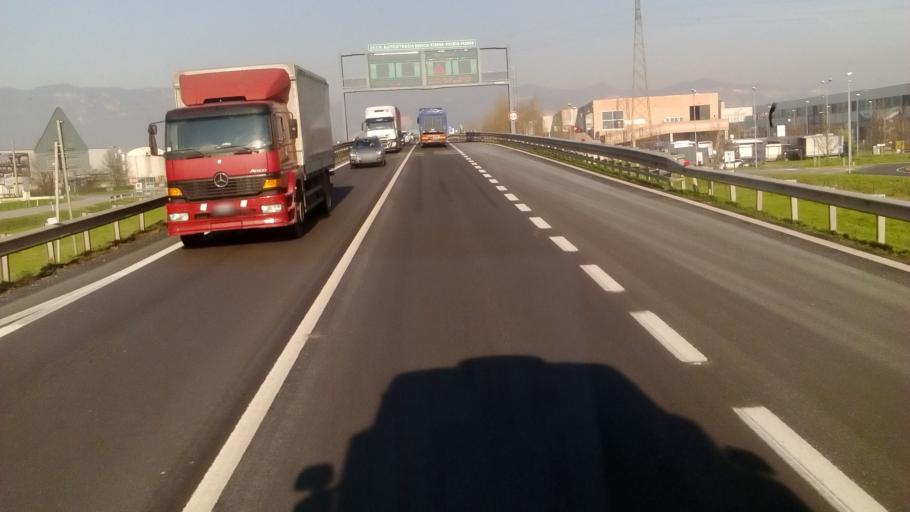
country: IT
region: Lombardy
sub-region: Provincia di Brescia
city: Castenedolo
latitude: 45.4786
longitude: 10.3184
